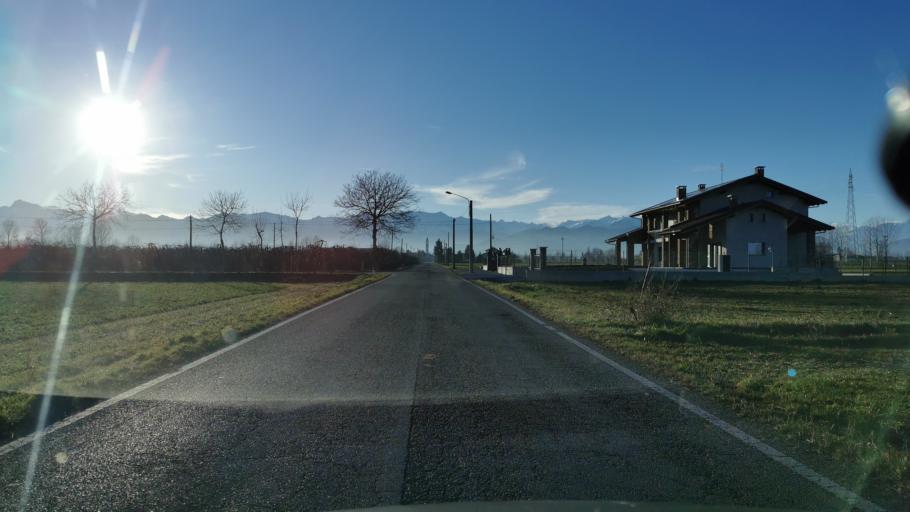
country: IT
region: Piedmont
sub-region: Provincia di Cuneo
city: Roata Rossi
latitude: 44.4574
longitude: 7.5021
